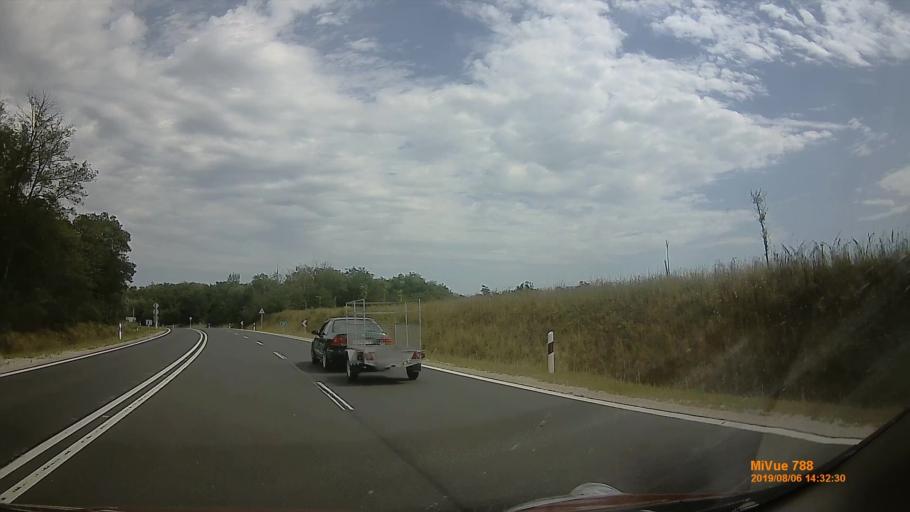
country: HU
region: Vas
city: Vasvar
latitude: 47.0967
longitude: 16.8955
